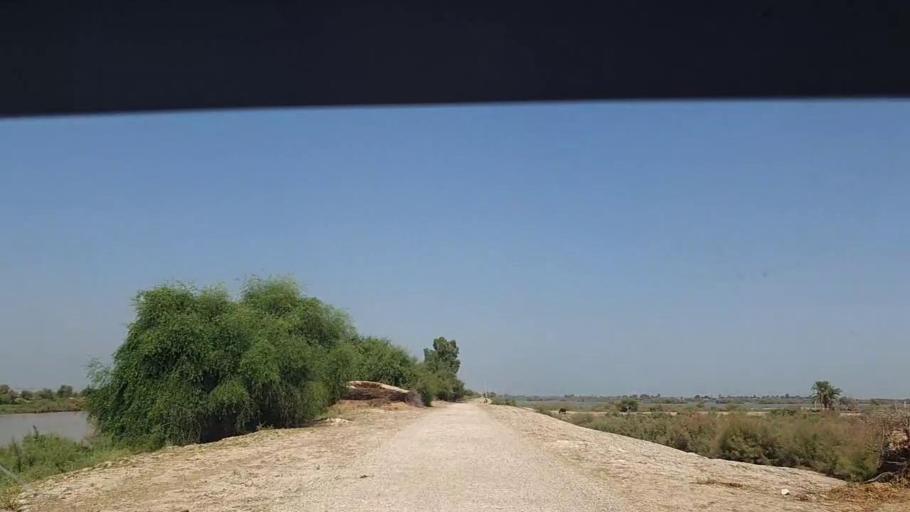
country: PK
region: Sindh
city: Kandhkot
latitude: 28.1936
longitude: 69.1678
